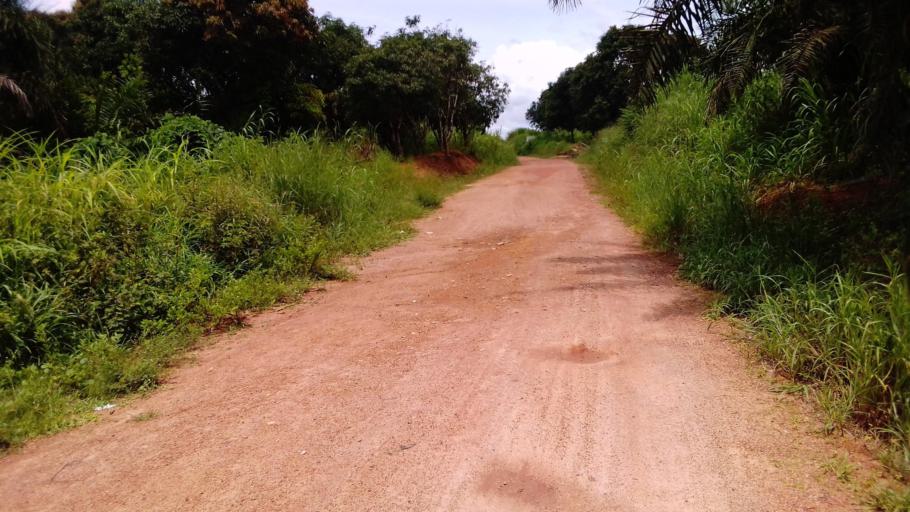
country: SL
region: Eastern Province
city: Koidu
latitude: 8.6612
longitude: -10.9413
